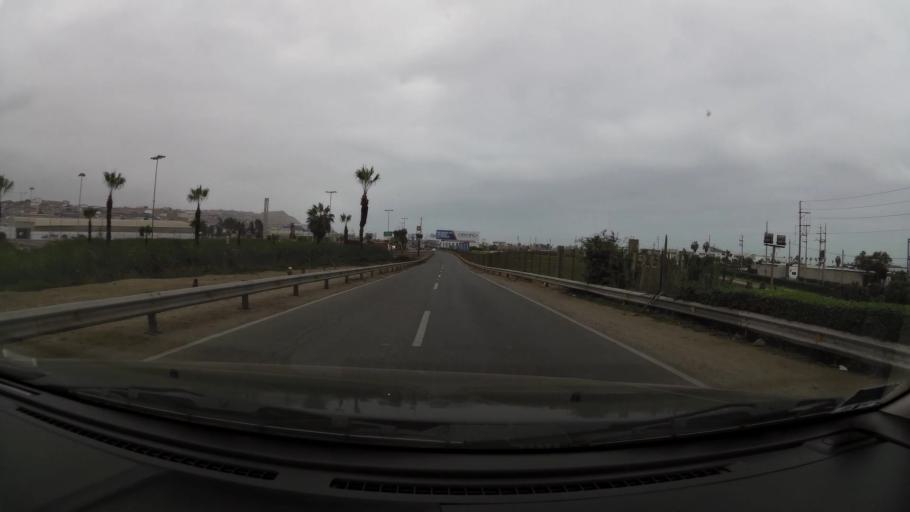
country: PE
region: Lima
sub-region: Lima
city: Surco
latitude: -12.2195
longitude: -76.9775
